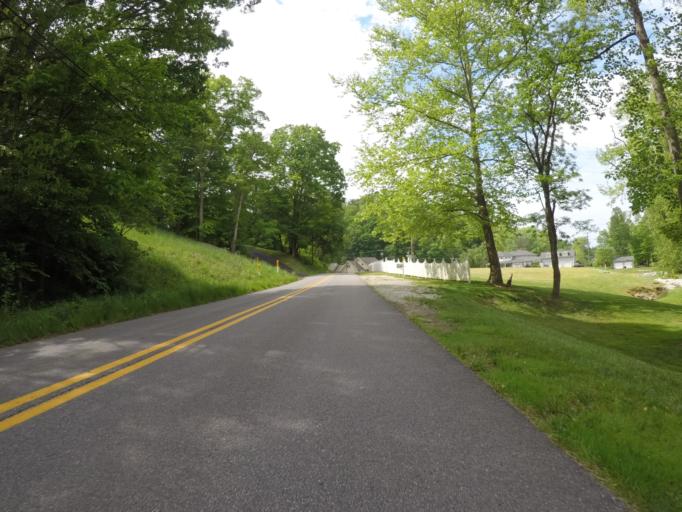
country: US
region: West Virginia
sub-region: Wayne County
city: Ceredo
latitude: 38.3500
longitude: -82.5628
